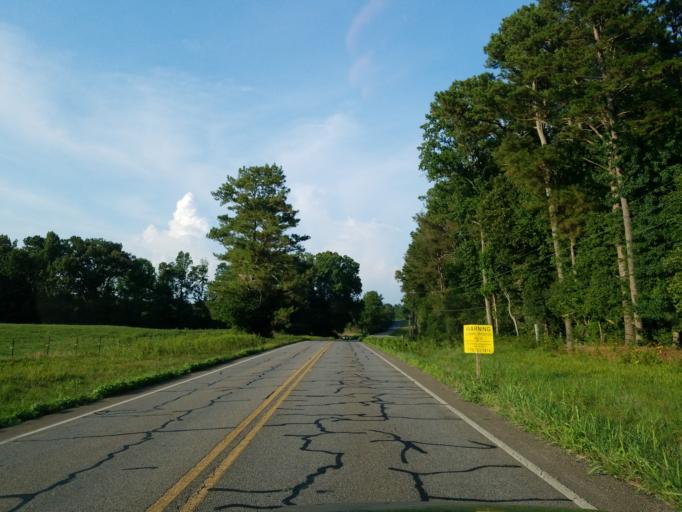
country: US
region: Georgia
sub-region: Pickens County
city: Jasper
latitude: 34.4869
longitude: -84.5785
